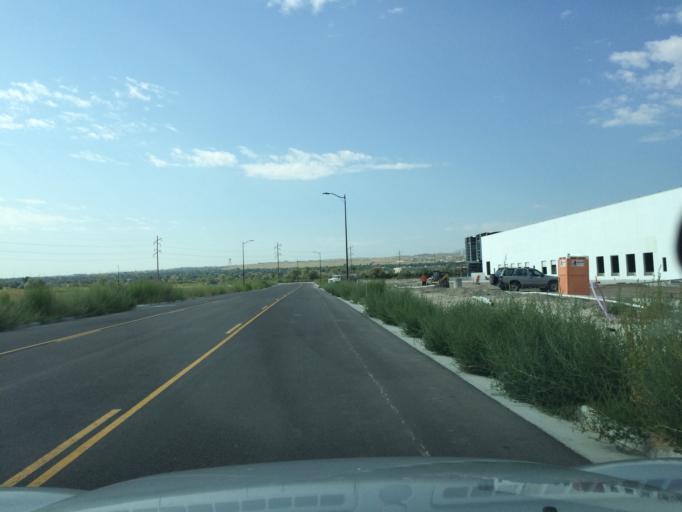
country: US
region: Utah
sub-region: Salt Lake County
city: Magna
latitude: 40.7172
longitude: -112.0526
